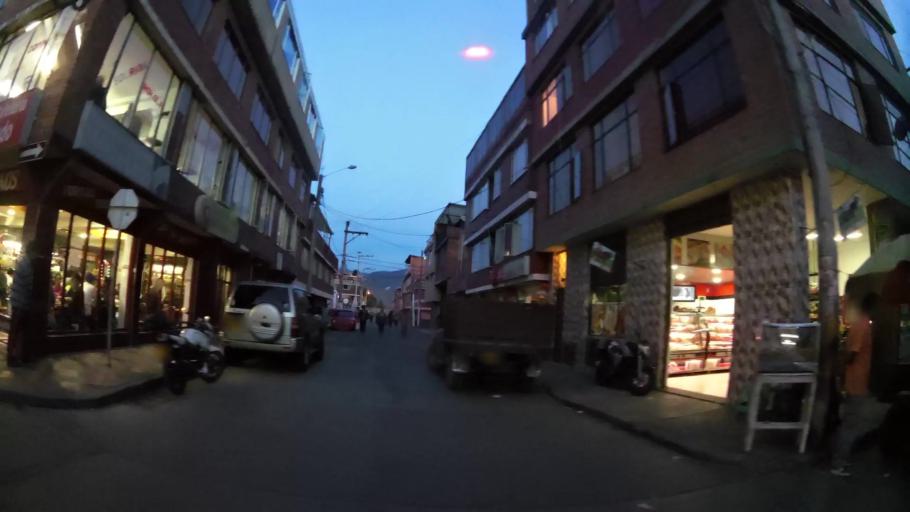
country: CO
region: Bogota D.C.
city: Bogota
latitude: 4.5549
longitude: -74.1370
